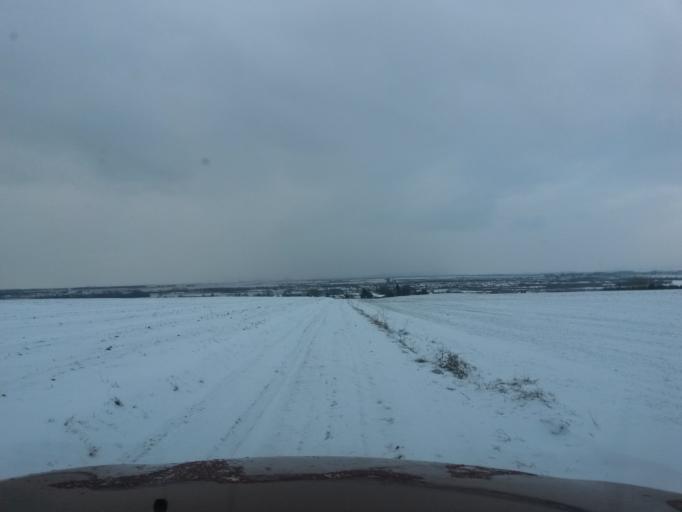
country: SK
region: Kosicky
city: Kosice
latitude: 48.6011
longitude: 21.3640
